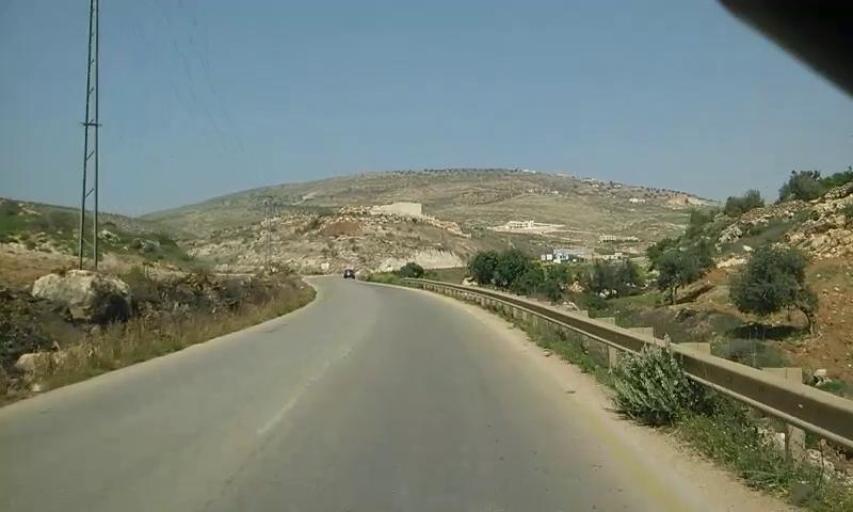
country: PS
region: West Bank
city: Tubas
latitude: 32.3012
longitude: 35.3644
